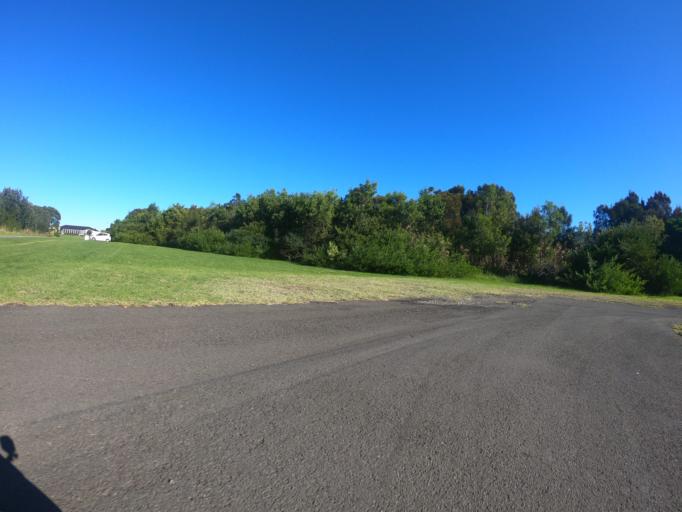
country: AU
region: New South Wales
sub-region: Wollongong
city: Corrimal
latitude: -34.3873
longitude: 150.9100
